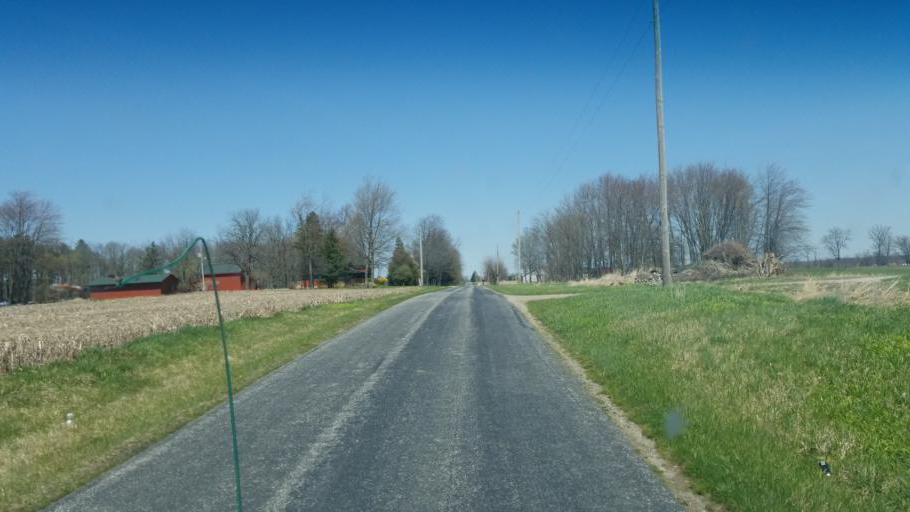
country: US
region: Ohio
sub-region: Huron County
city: New London
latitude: 41.0779
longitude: -82.4375
